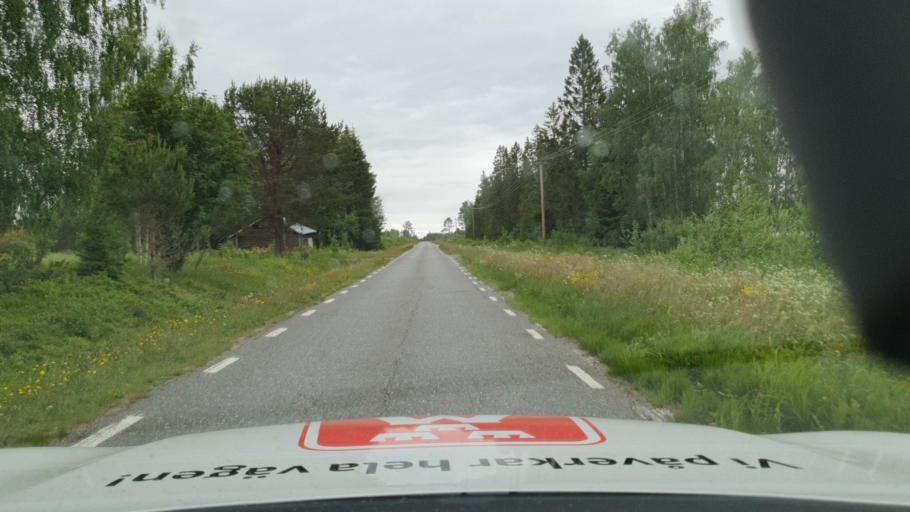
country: SE
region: Vaesterbotten
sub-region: Nordmalings Kommun
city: Nordmaling
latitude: 63.4415
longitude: 19.4685
